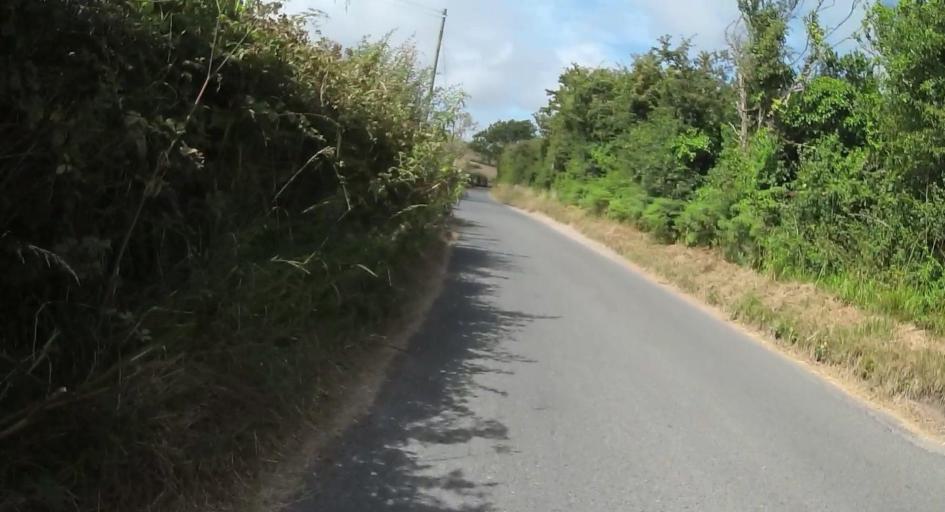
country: GB
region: England
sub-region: Dorset
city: Swanage
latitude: 50.6143
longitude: -1.9805
